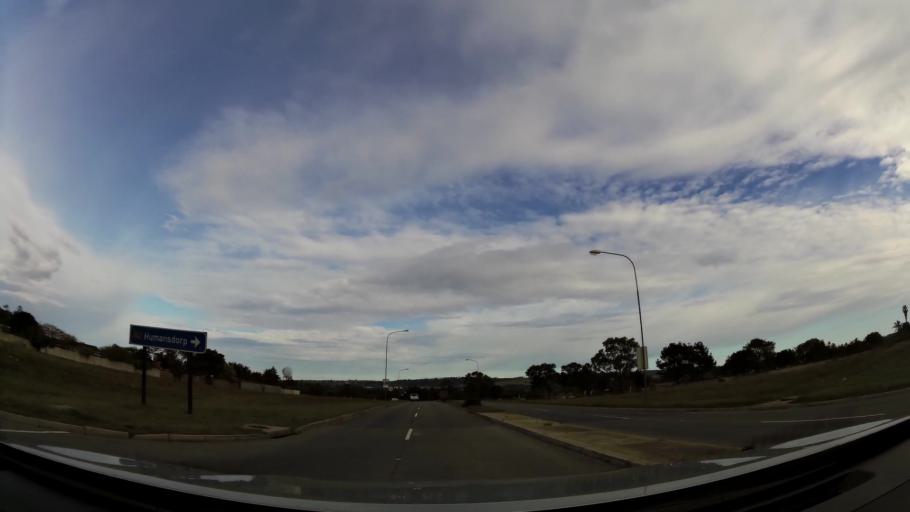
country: ZA
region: Eastern Cape
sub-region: Nelson Mandela Bay Metropolitan Municipality
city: Port Elizabeth
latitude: -33.9503
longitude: 25.5114
